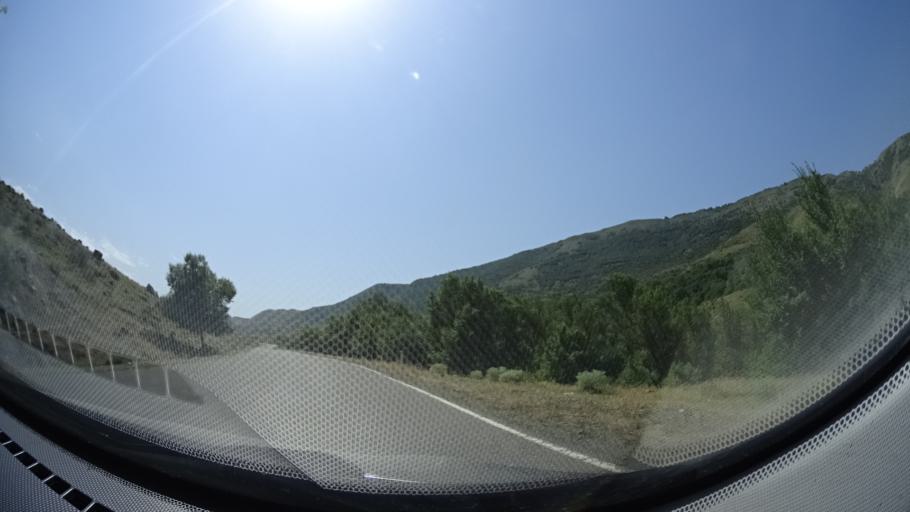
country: GE
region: Samtskhe-Javakheti
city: Aspindza
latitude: 41.5959
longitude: 43.1561
